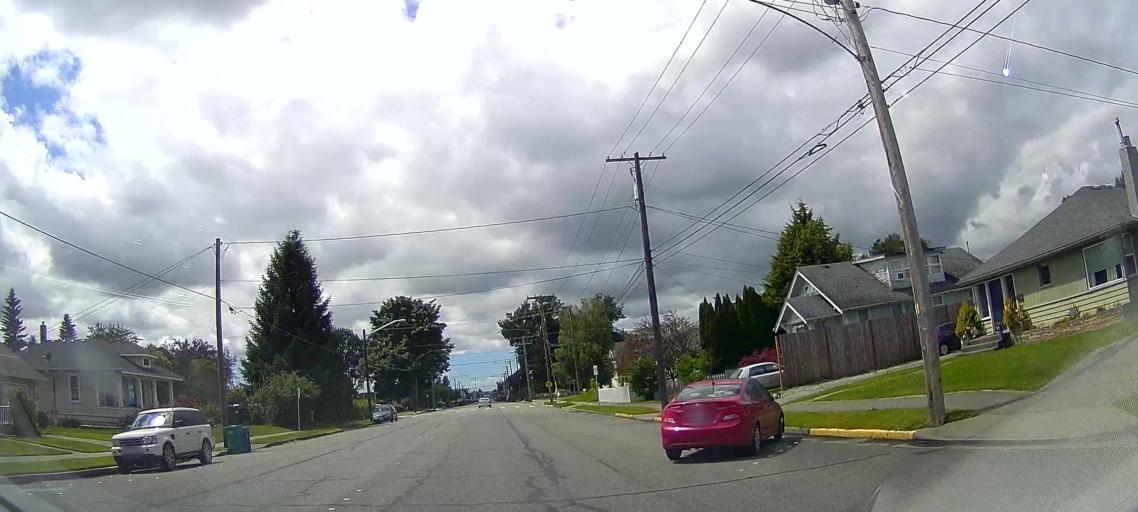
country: US
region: Washington
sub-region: Skagit County
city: Burlington
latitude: 48.4756
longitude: -122.3208
